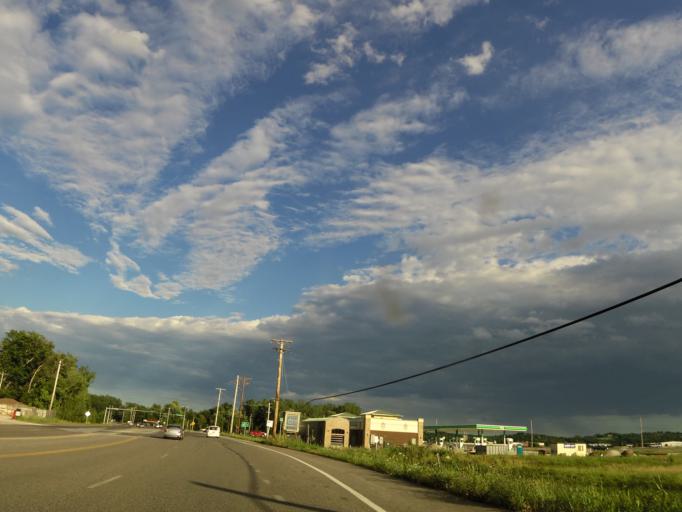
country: US
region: Missouri
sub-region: Saint Charles County
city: Weldon Spring
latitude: 38.6735
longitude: -90.6558
